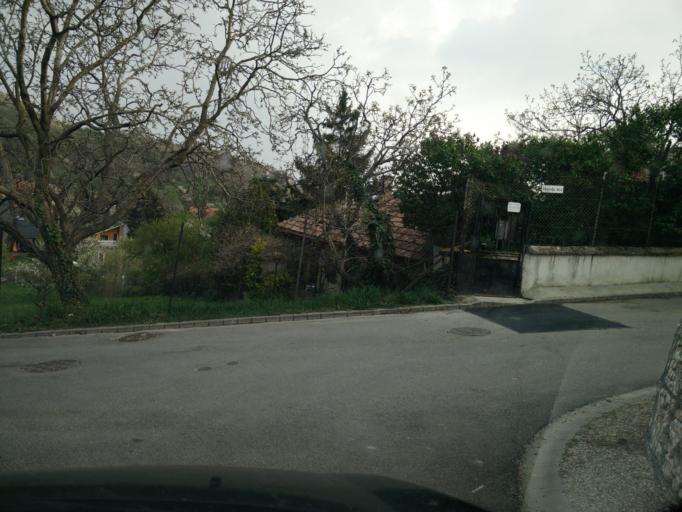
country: HU
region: Pest
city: Budaors
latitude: 47.4663
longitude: 18.9512
